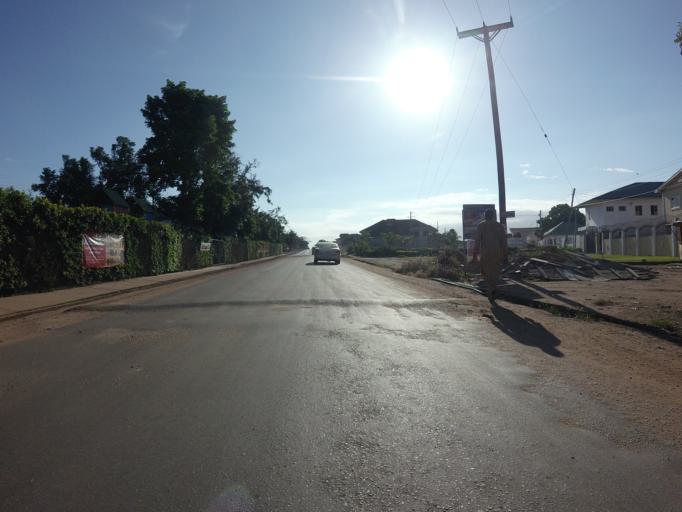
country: GH
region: Greater Accra
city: Tema
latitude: 5.6527
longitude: -0.0657
